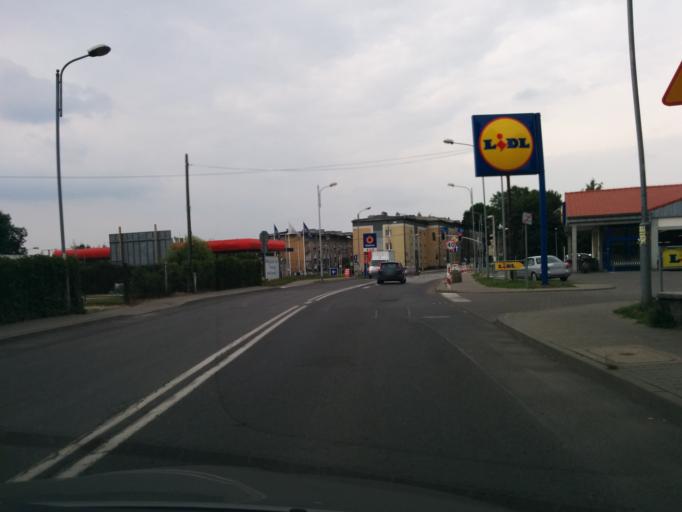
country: PL
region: Silesian Voivodeship
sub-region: Ruda Slaska
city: Ruda Slaska
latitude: 50.2701
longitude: 18.8326
